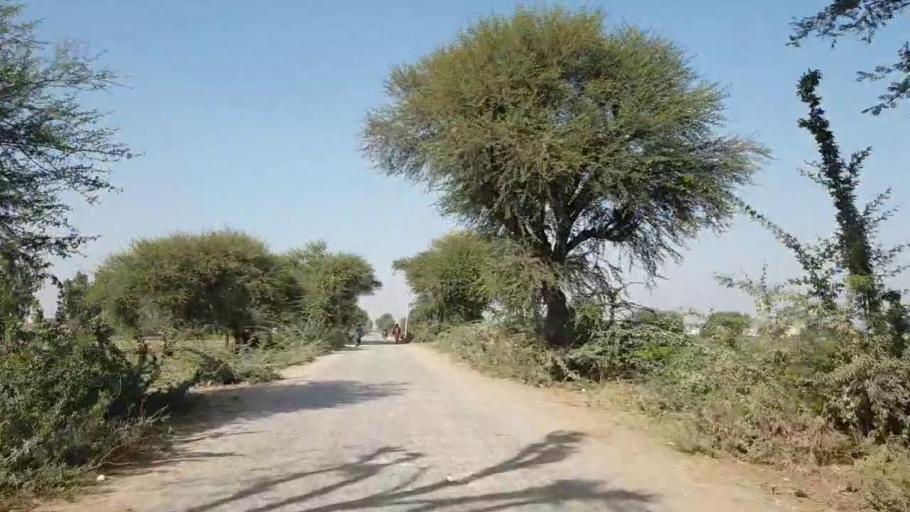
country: PK
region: Sindh
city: Digri
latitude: 25.1402
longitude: 69.1117
